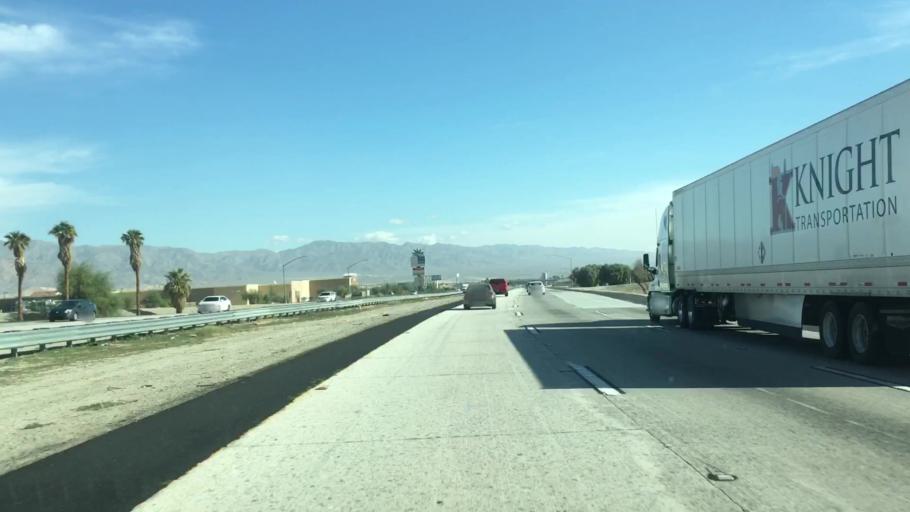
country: US
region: California
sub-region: Riverside County
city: Indio
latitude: 33.7394
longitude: -116.2333
